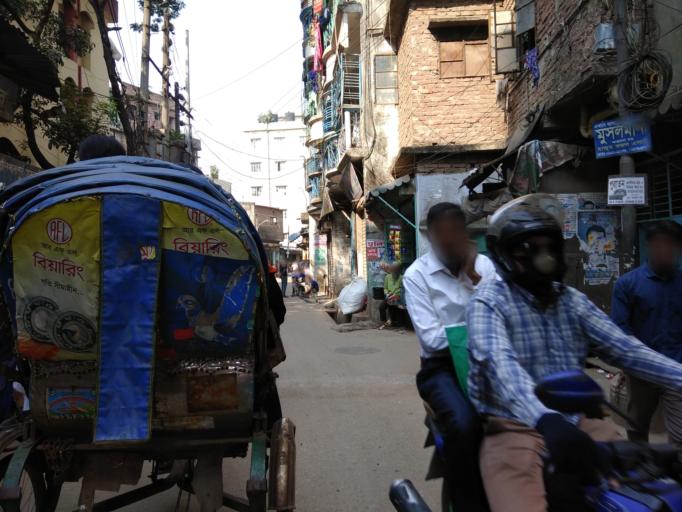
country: BD
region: Dhaka
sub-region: Dhaka
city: Dhaka
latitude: 23.7214
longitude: 90.4007
